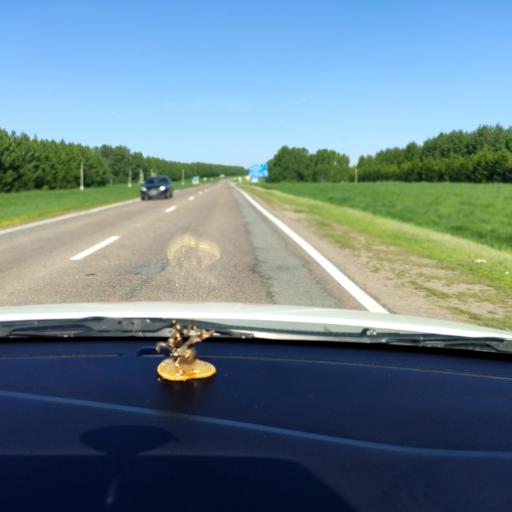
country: RU
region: Tatarstan
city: Vysokaya Gora
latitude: 56.0325
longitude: 49.2405
